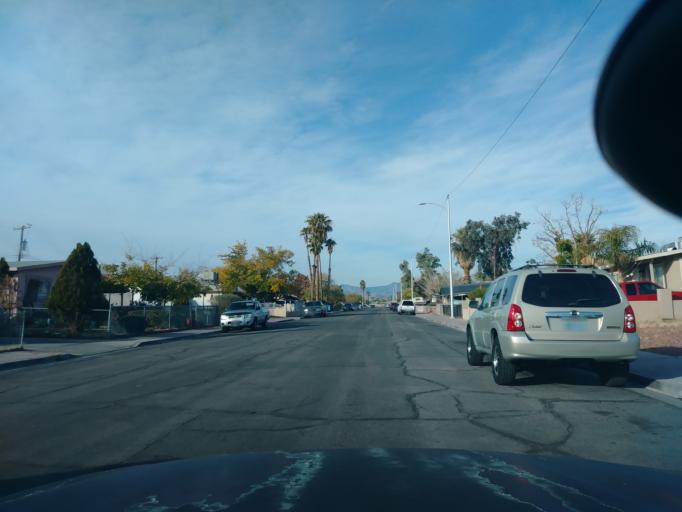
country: US
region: Nevada
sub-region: Clark County
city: Spring Valley
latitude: 36.1636
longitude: -115.2300
